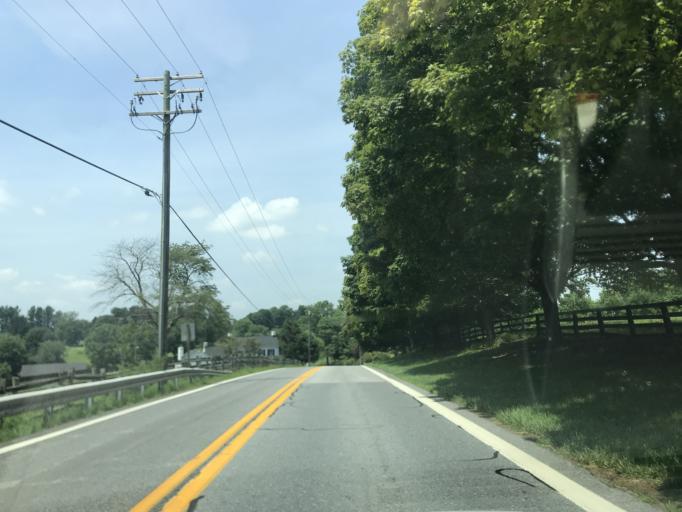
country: US
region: Maryland
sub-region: Carroll County
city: Hampstead
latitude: 39.5937
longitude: -76.7388
